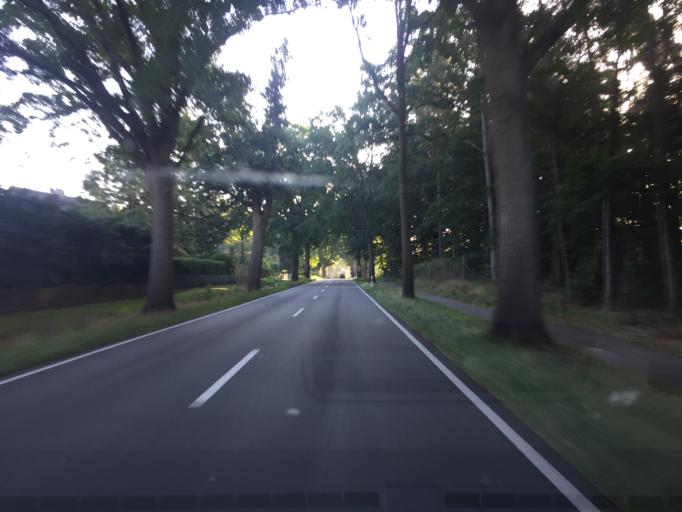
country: DE
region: Lower Saxony
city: Bohme
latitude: 52.8173
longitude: 9.4471
